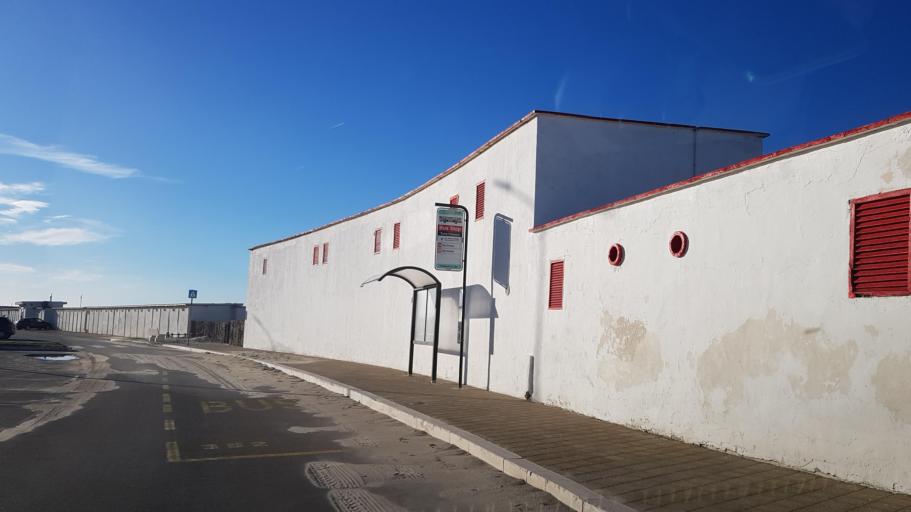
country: IT
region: Apulia
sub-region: Provincia di Lecce
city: Giorgilorio
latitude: 40.4676
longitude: 18.1942
